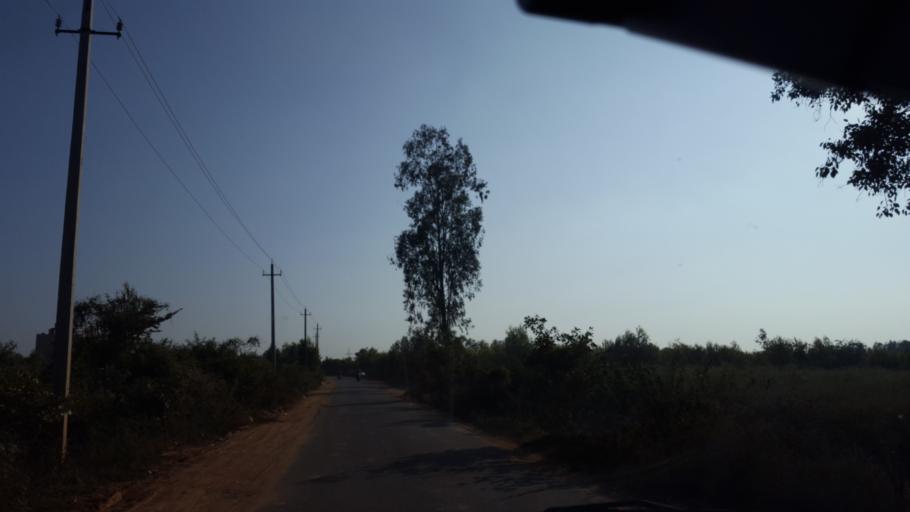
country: IN
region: Karnataka
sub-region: Bangalore Rural
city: Hoskote
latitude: 12.9252
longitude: 77.7565
